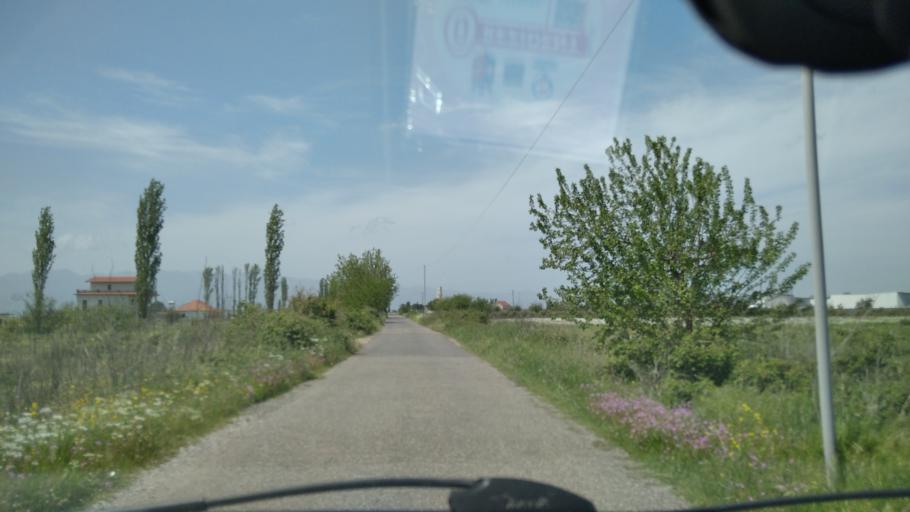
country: AL
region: Shkoder
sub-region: Rrethi i Malesia e Madhe
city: Gruemire
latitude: 42.1425
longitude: 19.5104
